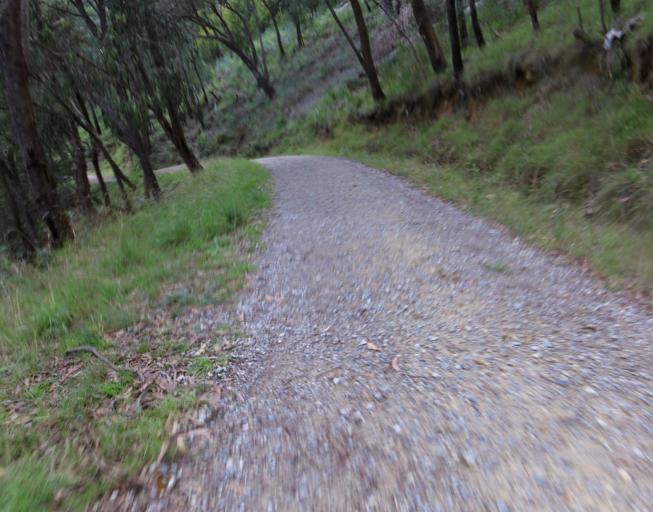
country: AU
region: Victoria
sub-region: Yarra Ranges
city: Montrose
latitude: -37.8340
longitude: 145.3435
